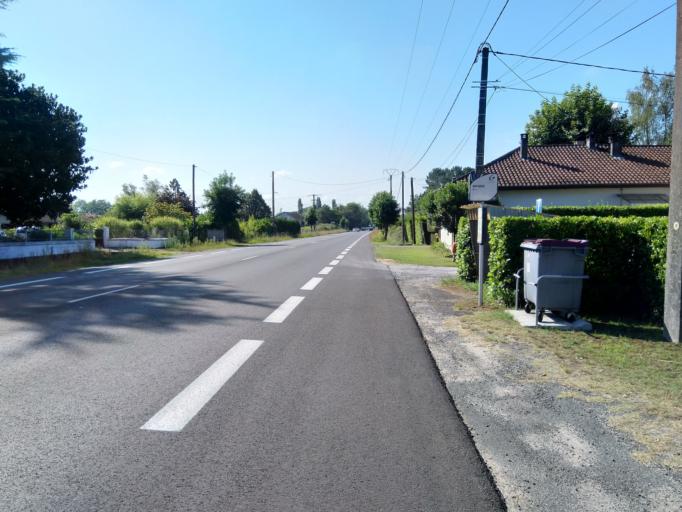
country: FR
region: Aquitaine
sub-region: Departement des Landes
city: Saint-Paul-les-Dax
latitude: 43.7534
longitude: -1.0590
